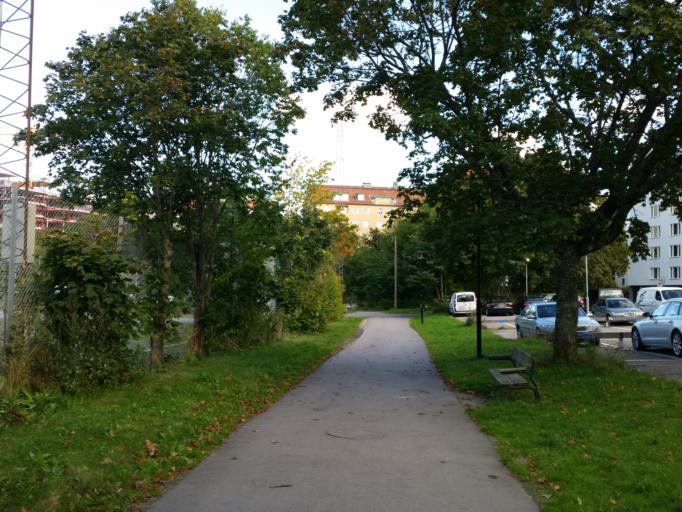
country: SE
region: Stockholm
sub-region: Solna Kommun
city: Solna
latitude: 59.3692
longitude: 17.9961
